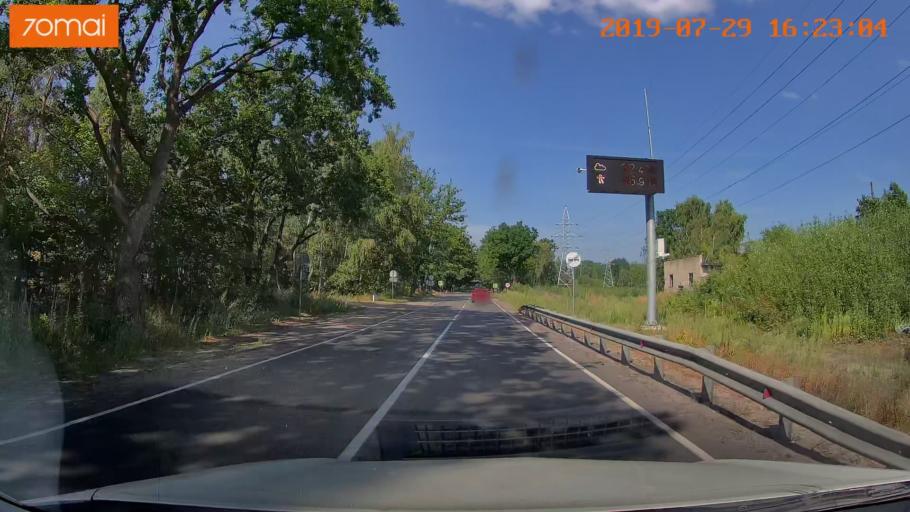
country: RU
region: Kaliningrad
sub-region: Gorod Kaliningrad
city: Baltiysk
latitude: 54.7031
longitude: 19.9438
